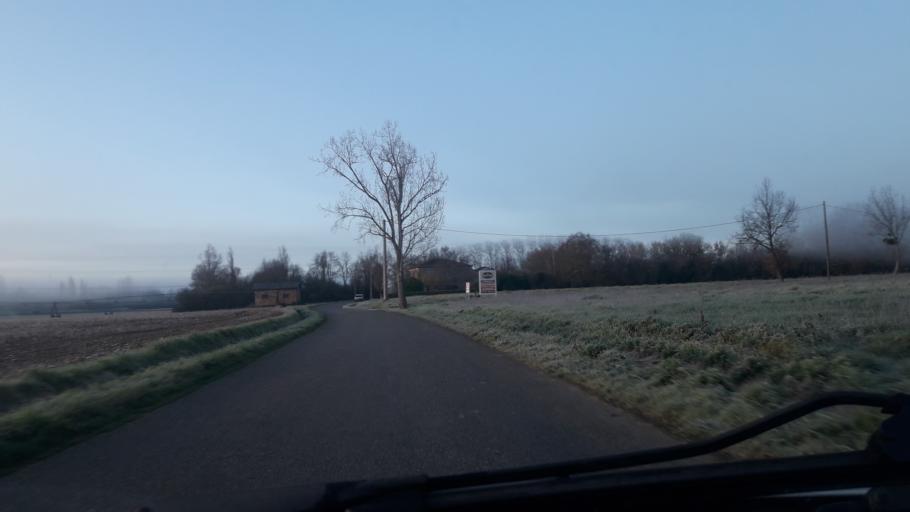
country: FR
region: Midi-Pyrenees
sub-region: Departement de la Haute-Garonne
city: Berat
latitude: 43.3927
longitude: 1.1756
